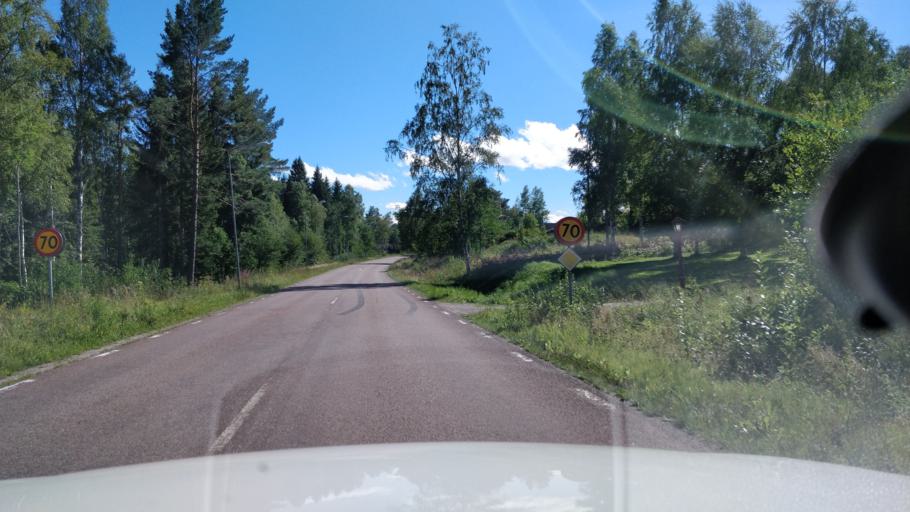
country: SE
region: Dalarna
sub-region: Faluns Kommun
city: Bjursas
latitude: 60.7444
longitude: 15.4692
